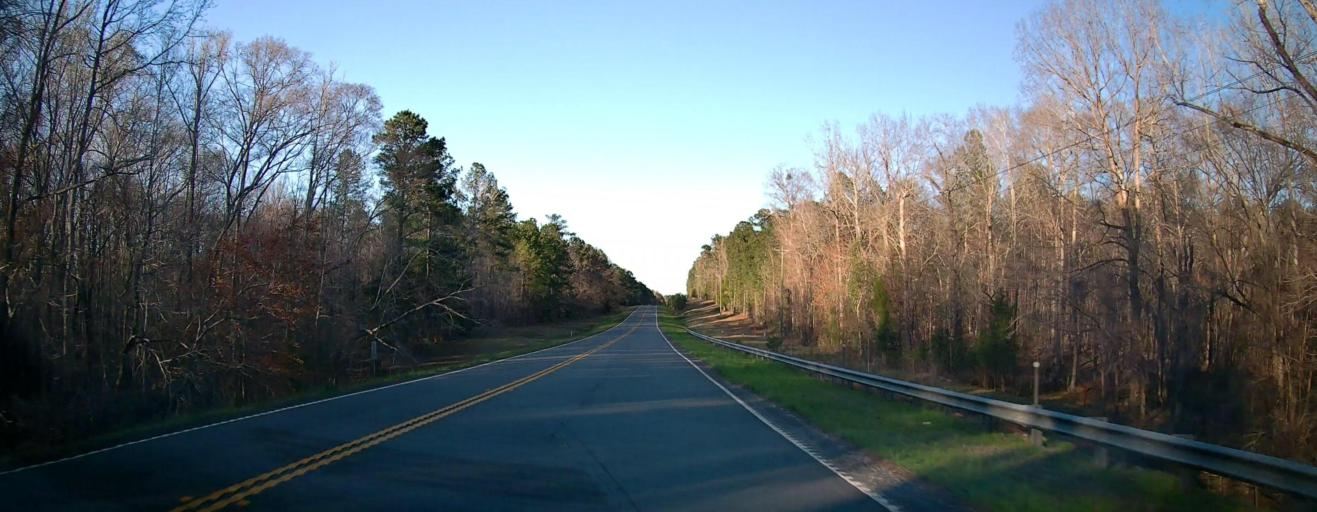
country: US
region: Georgia
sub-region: Talbot County
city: Talbotton
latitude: 32.6122
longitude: -84.5512
